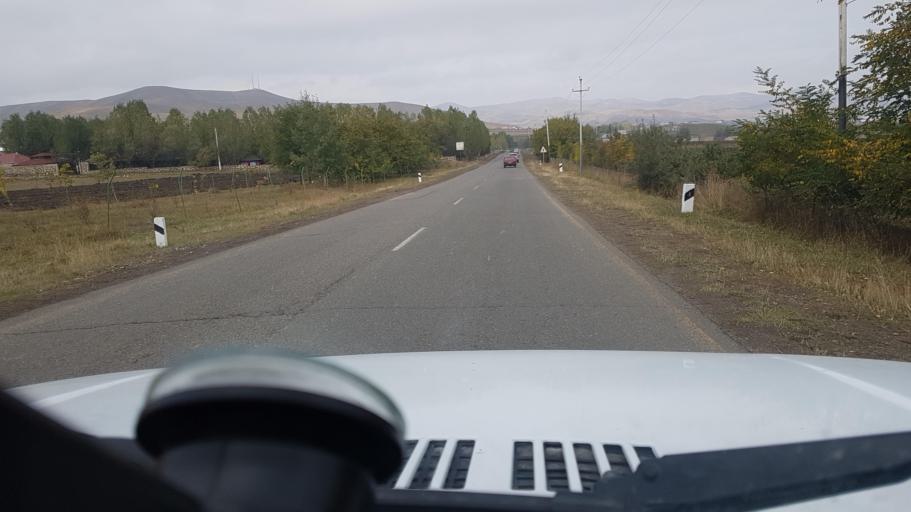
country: AZ
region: Gadabay Rayon
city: Ariqdam
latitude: 40.6275
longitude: 45.8156
